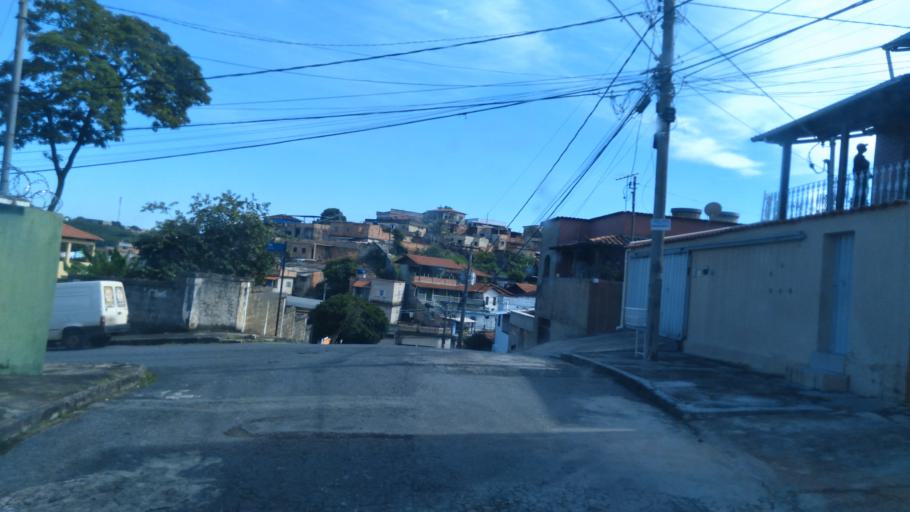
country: BR
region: Minas Gerais
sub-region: Belo Horizonte
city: Belo Horizonte
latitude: -19.8654
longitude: -43.9031
